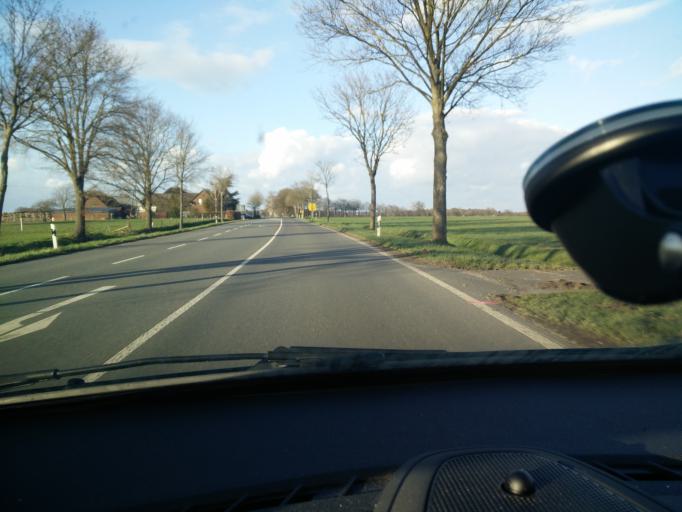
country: DE
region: North Rhine-Westphalia
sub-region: Regierungsbezirk Munster
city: Rhede
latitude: 51.7399
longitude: 6.7287
